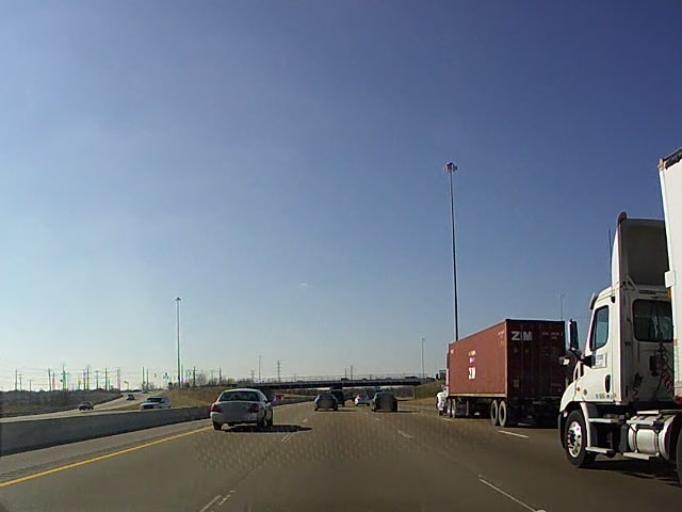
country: US
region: Tennessee
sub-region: Shelby County
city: Germantown
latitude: 35.0788
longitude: -89.9060
